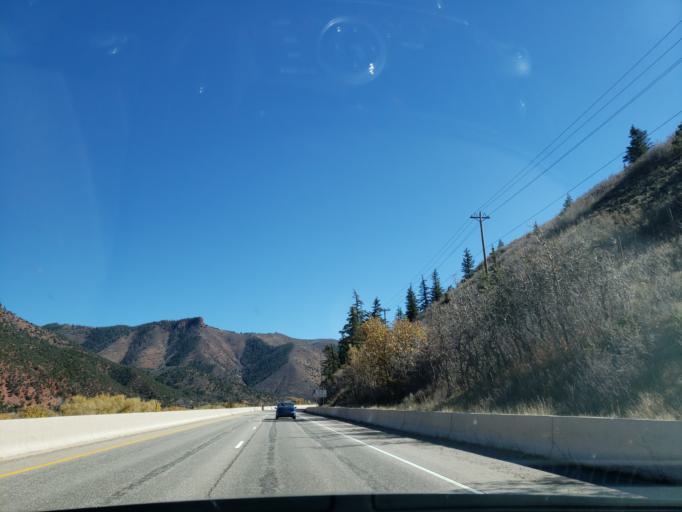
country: US
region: Colorado
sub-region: Eagle County
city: Basalt
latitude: 39.3279
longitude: -106.9617
